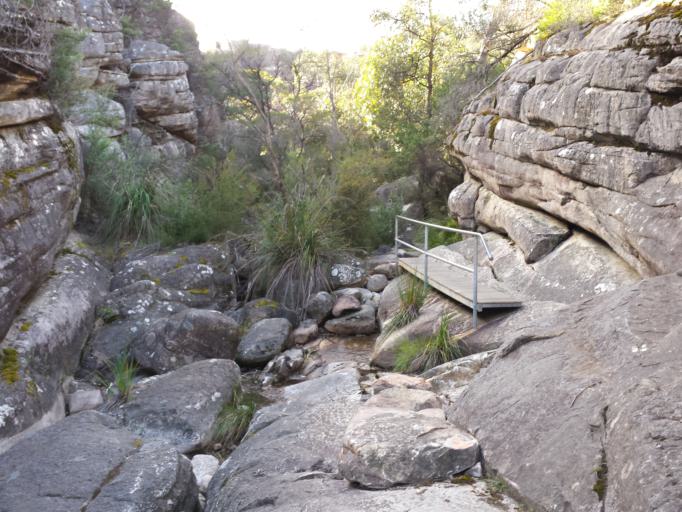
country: AU
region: Victoria
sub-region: Northern Grampians
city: Stawell
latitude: -37.1513
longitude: 142.5041
